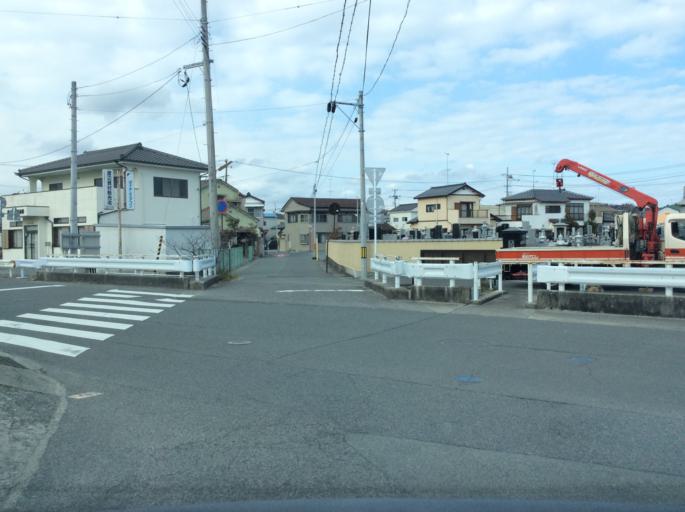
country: JP
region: Fukushima
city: Iwaki
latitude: 36.9528
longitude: 140.9059
